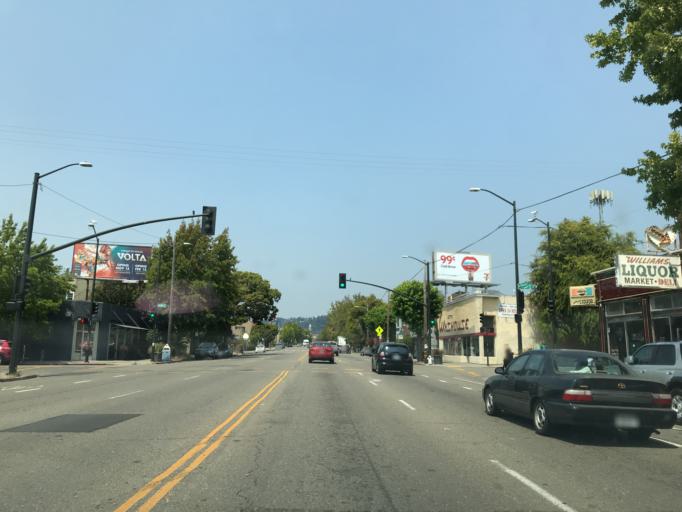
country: US
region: California
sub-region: Alameda County
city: Emeryville
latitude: 37.8446
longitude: -122.2613
